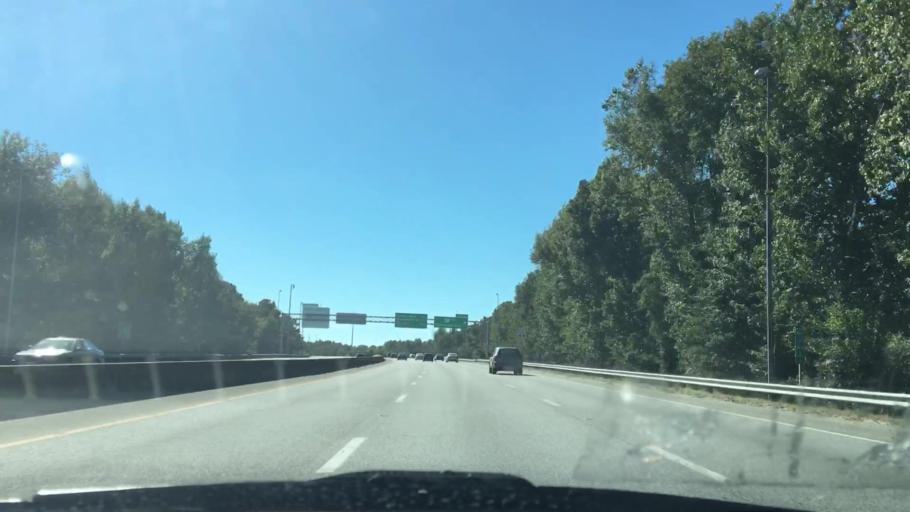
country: US
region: Virginia
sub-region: City of Portsmouth
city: Portsmouth Heights
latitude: 36.8200
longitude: -76.3416
